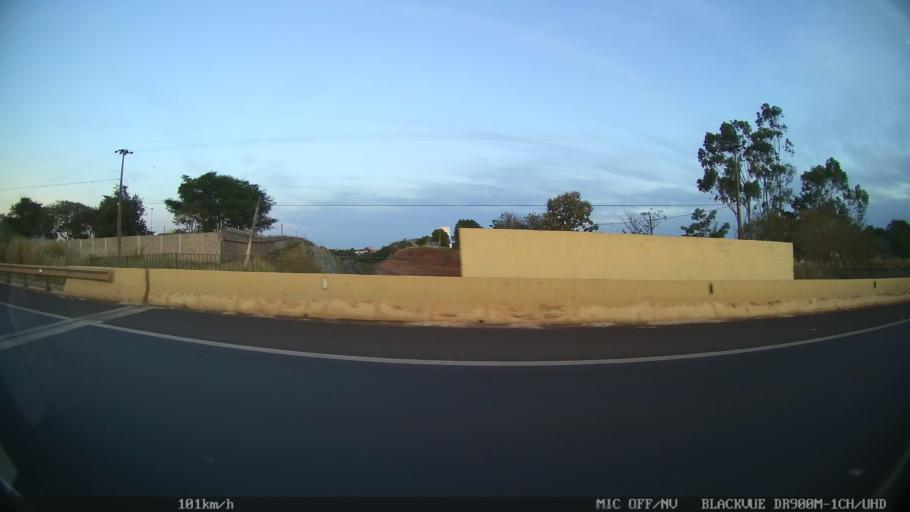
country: BR
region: Sao Paulo
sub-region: Catanduva
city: Catanduva
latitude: -21.1185
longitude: -48.9849
